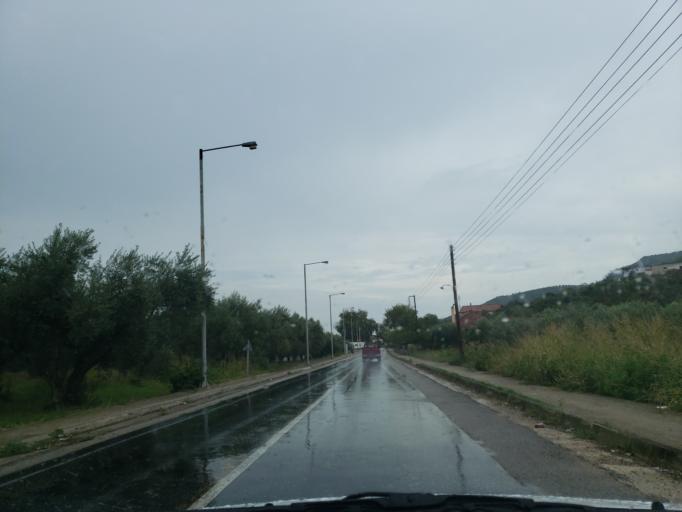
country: GR
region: Central Greece
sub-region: Nomos Fthiotidos
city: Anthili
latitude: 38.7993
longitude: 22.4738
